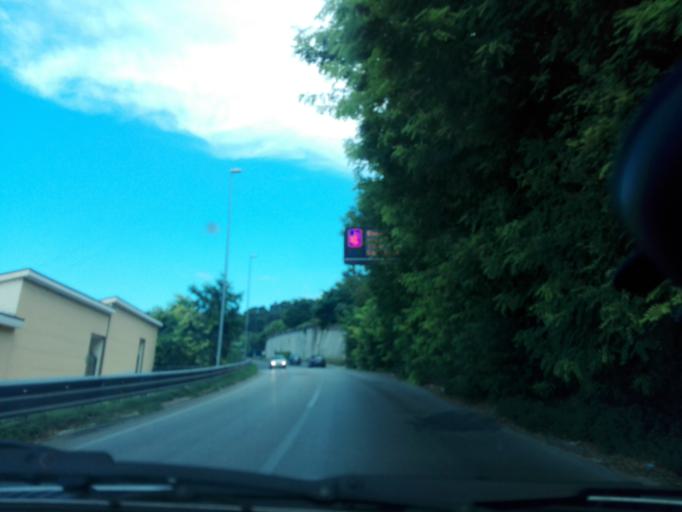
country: IT
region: Abruzzo
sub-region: Provincia di Pescara
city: Montesilvano Marina
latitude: 42.4994
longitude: 14.1410
